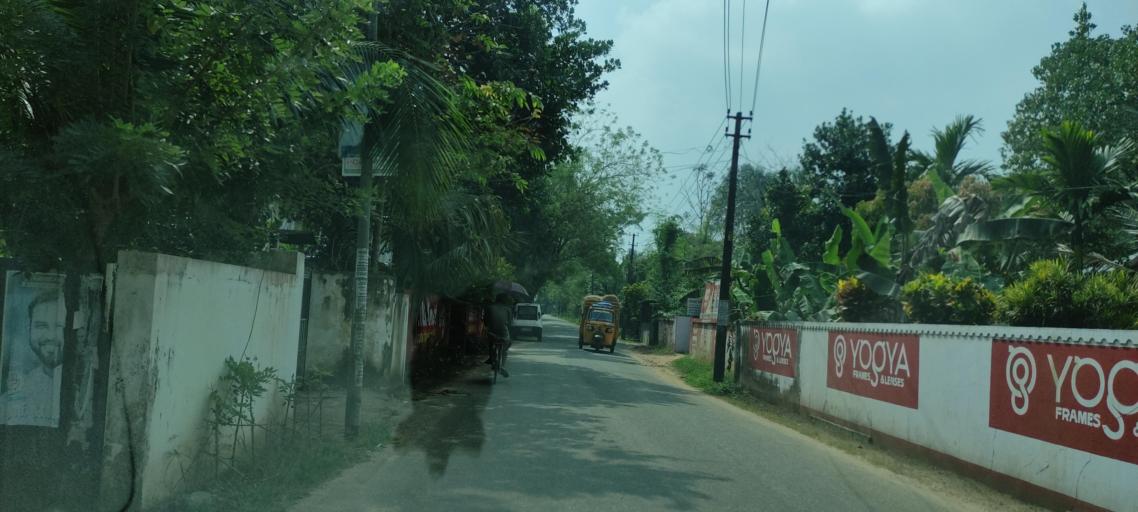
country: IN
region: Kerala
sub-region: Alappuzha
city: Shertallai
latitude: 9.6444
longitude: 76.3550
